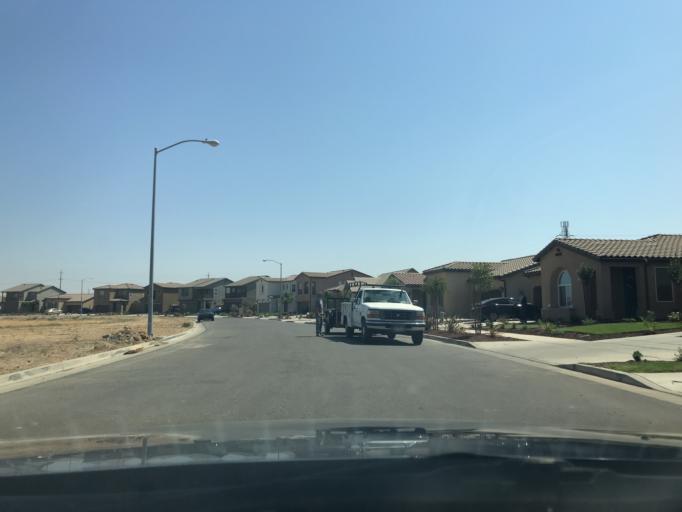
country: US
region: California
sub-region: Merced County
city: Merced
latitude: 37.3481
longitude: -120.4717
